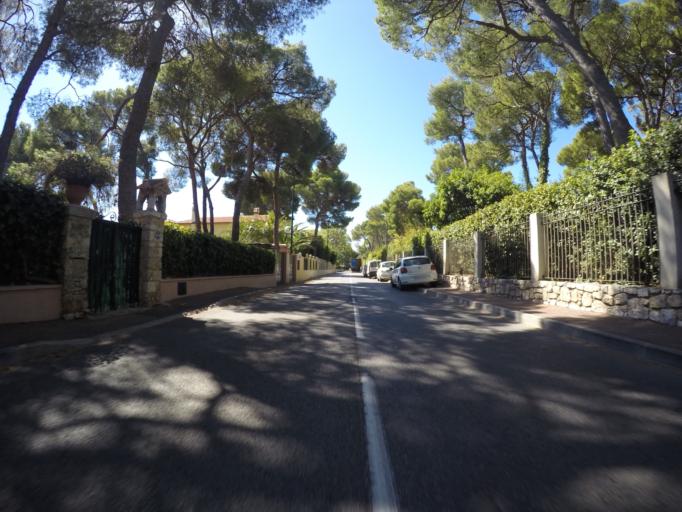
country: FR
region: Provence-Alpes-Cote d'Azur
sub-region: Departement des Alpes-Maritimes
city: Saint-Jean-Cap-Ferrat
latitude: 43.6818
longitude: 7.3334
